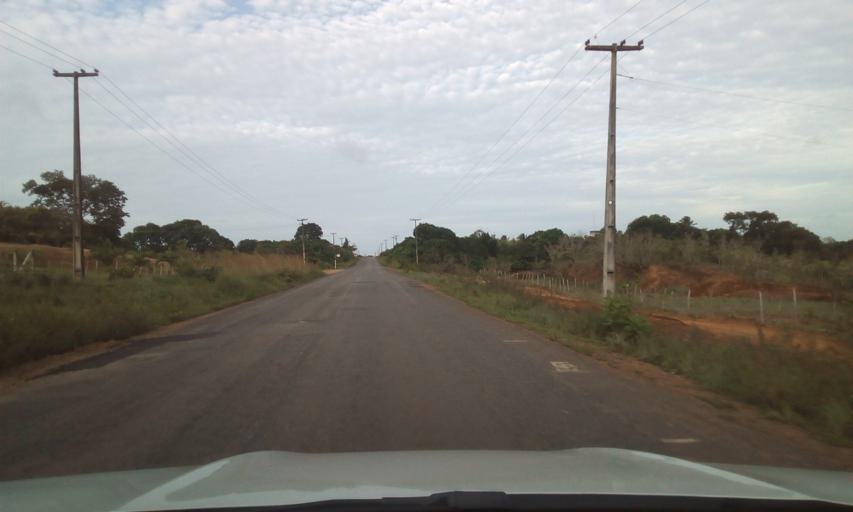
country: BR
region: Paraiba
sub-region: Conde
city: Conde
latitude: -7.2757
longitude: -34.8638
